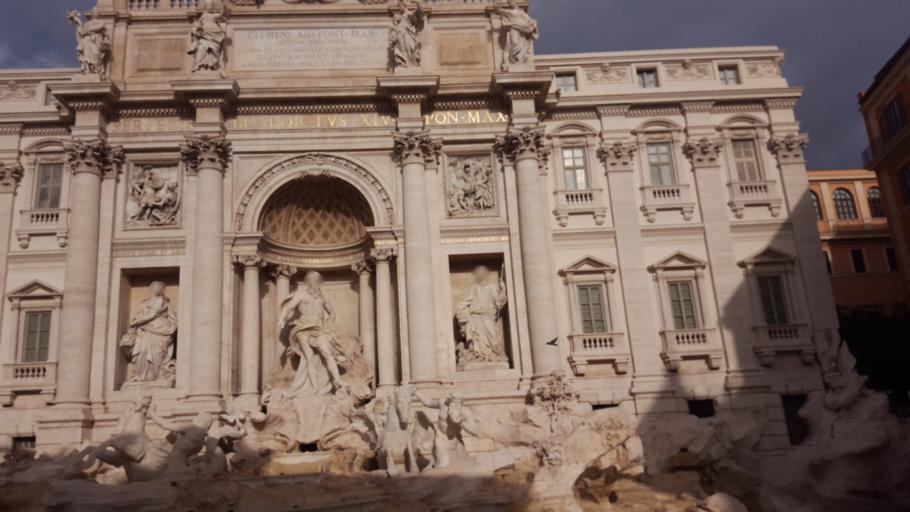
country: IT
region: Latium
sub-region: Citta metropolitana di Roma Capitale
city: Rome
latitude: 41.9011
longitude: 12.4835
